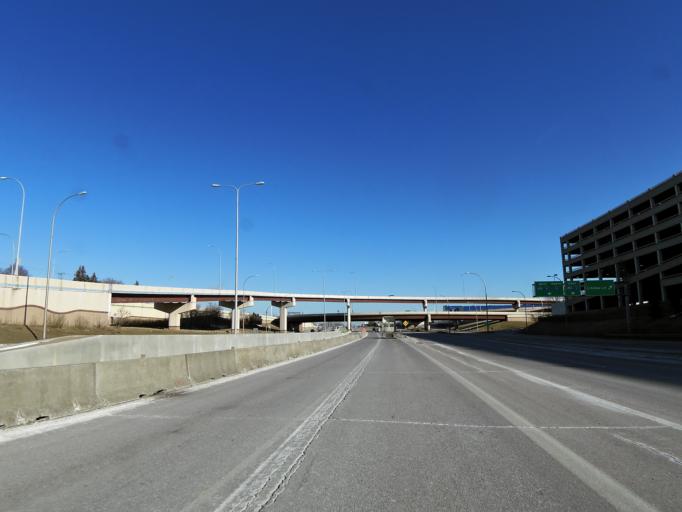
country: US
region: Minnesota
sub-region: Hennepin County
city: Richfield
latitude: 44.8547
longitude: -93.2470
